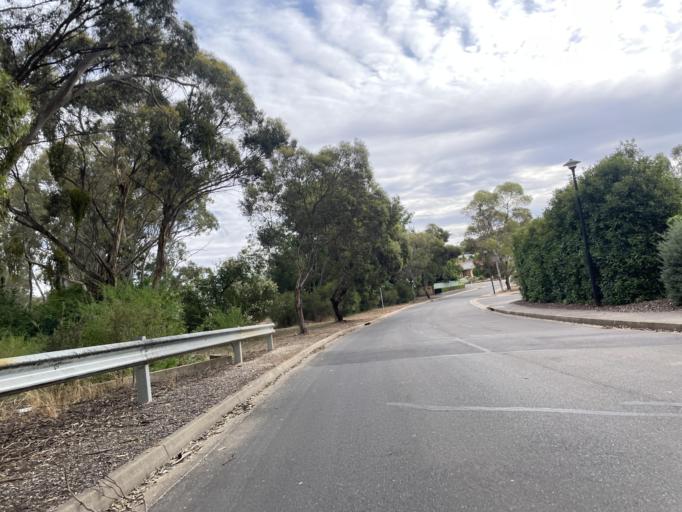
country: AU
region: South Australia
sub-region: Clare and Gilbert Valleys
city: Clare
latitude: -33.8438
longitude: 138.6132
